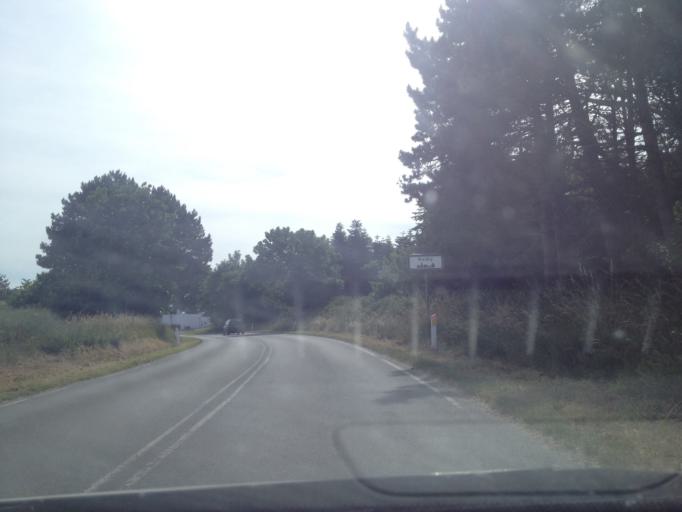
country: DK
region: Central Jutland
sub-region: Samso Kommune
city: Tranebjerg
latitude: 55.8016
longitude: 10.5597
